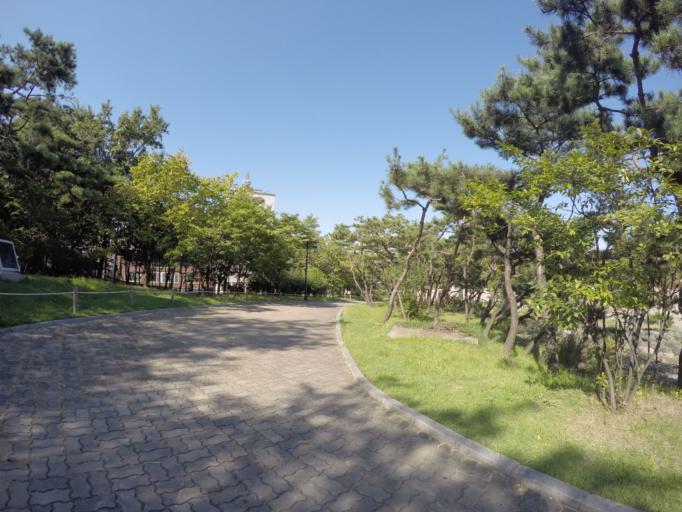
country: KR
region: Seoul
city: Seoul
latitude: 37.5586
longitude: 126.9928
